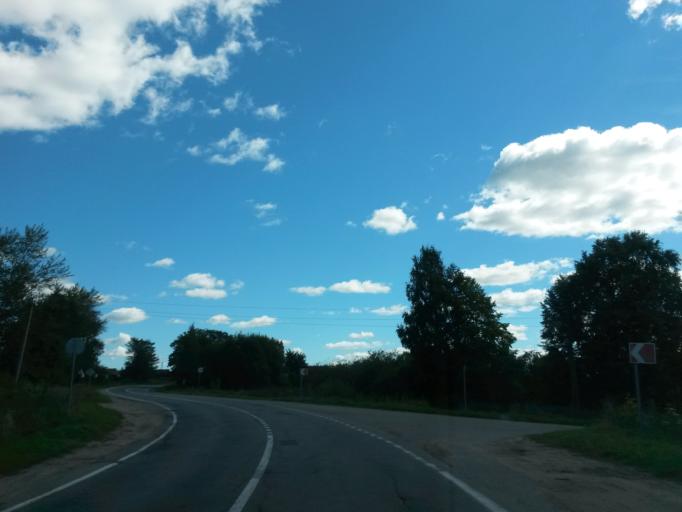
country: RU
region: Jaroslavl
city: Konstantinovskiy
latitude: 57.8456
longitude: 39.6411
